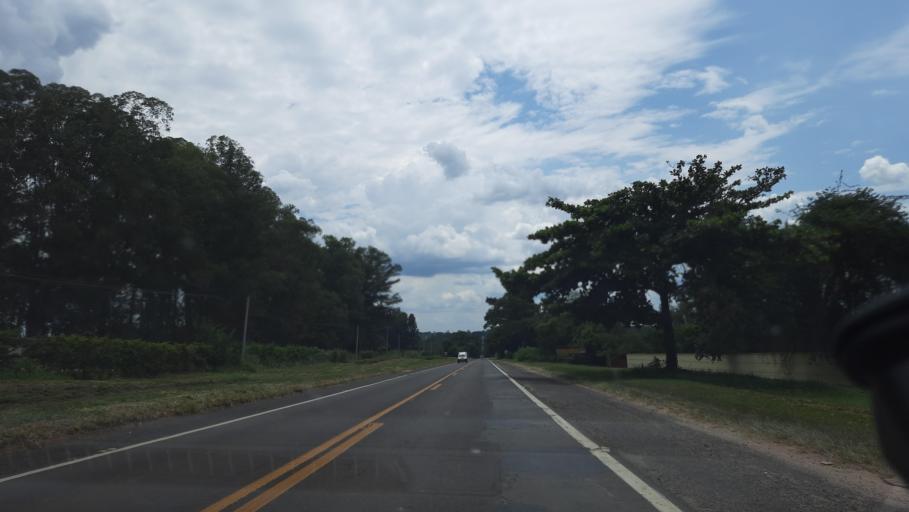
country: BR
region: Sao Paulo
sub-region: Mococa
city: Mococa
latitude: -21.5060
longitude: -47.0510
